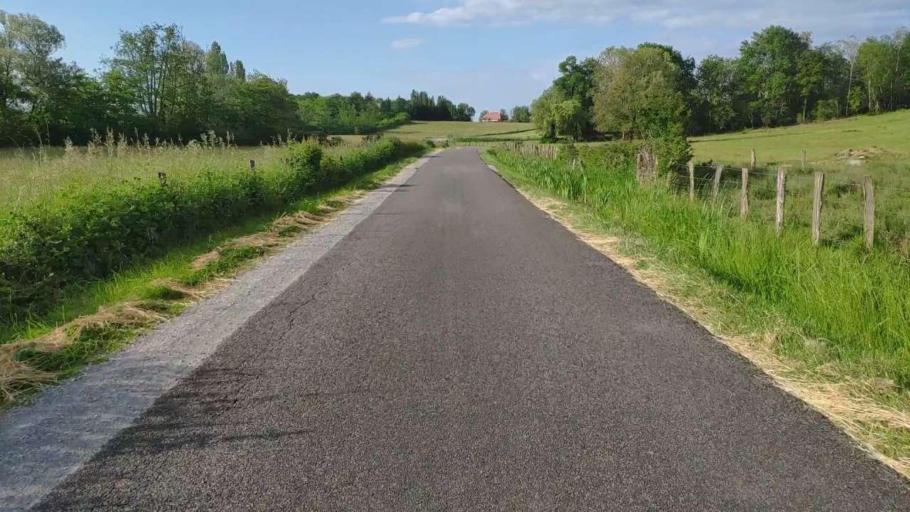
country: FR
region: Franche-Comte
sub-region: Departement du Jura
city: Bletterans
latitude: 46.7542
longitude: 5.4489
